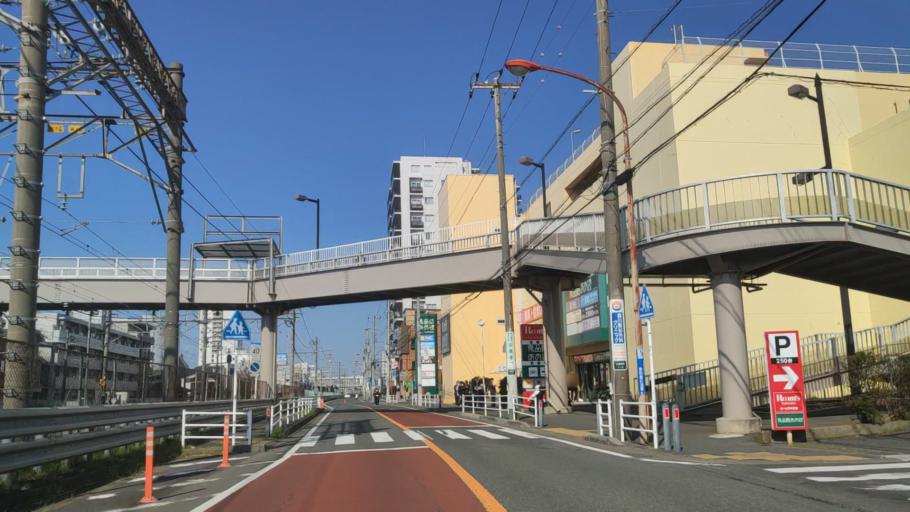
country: JP
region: Kanagawa
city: Fujisawa
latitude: 35.3373
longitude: 139.4536
